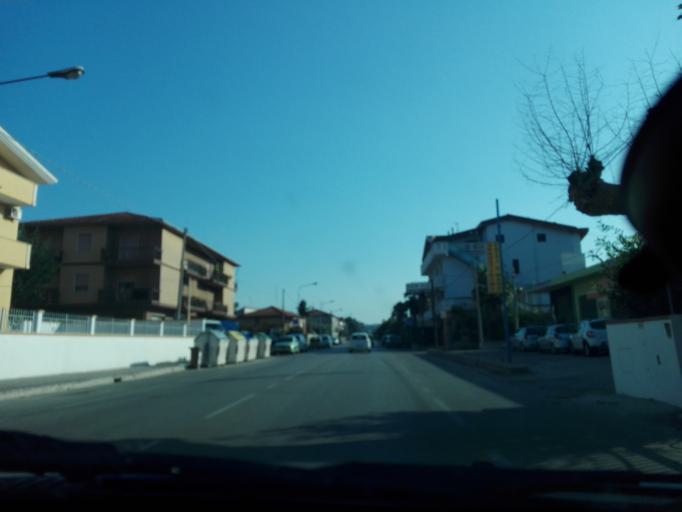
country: IT
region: Abruzzo
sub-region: Provincia di Pescara
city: Cappelle sul Tavo
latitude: 42.4912
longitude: 14.1231
